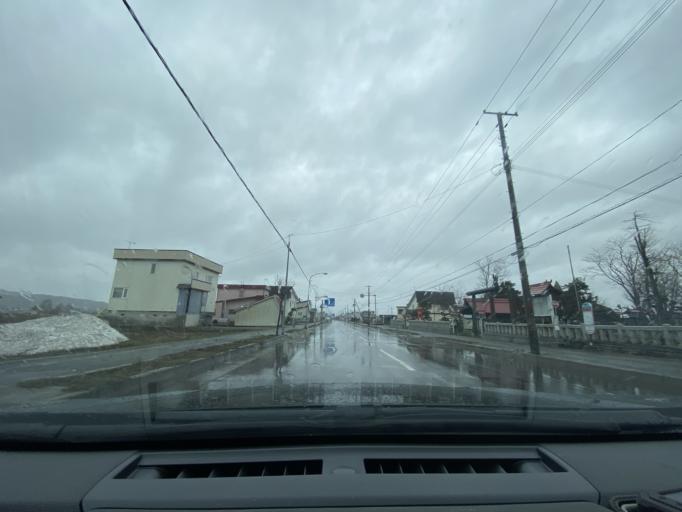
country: JP
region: Hokkaido
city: Fukagawa
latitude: 43.8087
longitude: 142.0276
